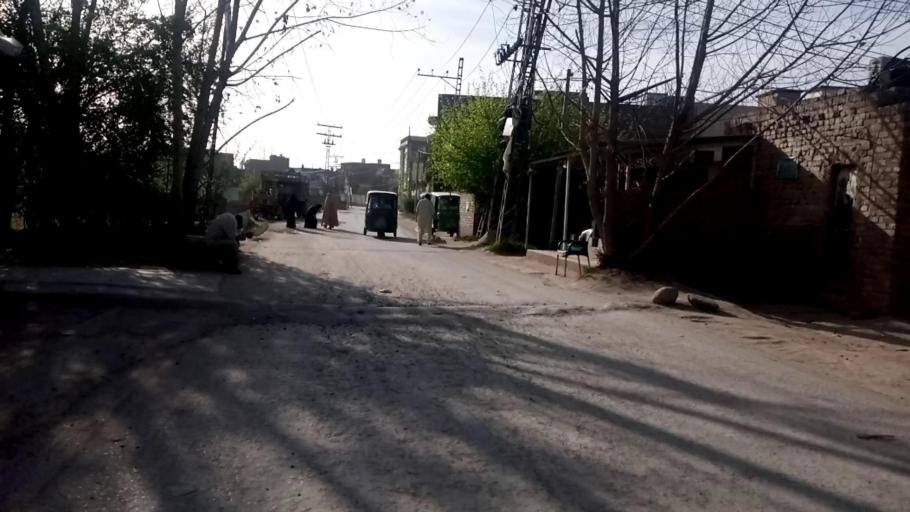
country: PK
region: Khyber Pakhtunkhwa
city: Peshawar
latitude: 34.0114
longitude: 71.6129
